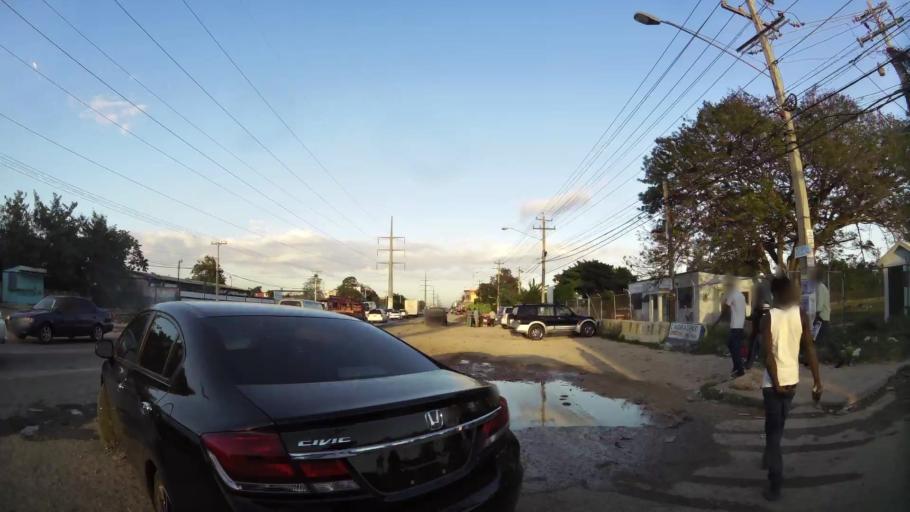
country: DO
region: Santo Domingo
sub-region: Santo Domingo
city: Santo Domingo Este
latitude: 18.4913
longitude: -69.8175
